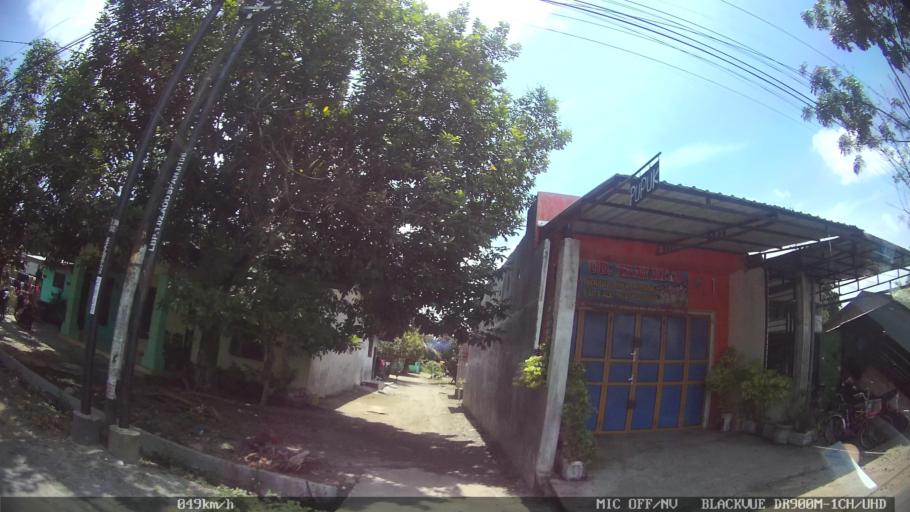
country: ID
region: North Sumatra
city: Binjai
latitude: 3.5968
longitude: 98.5182
